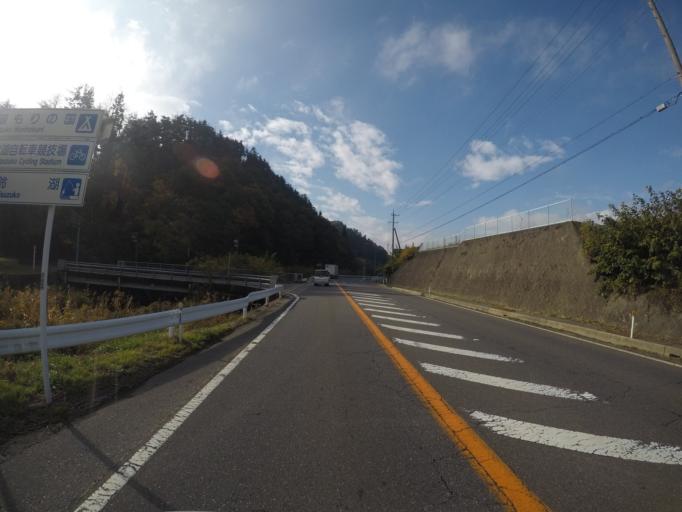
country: JP
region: Nagano
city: Matsumoto
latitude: 36.2880
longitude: 137.9918
